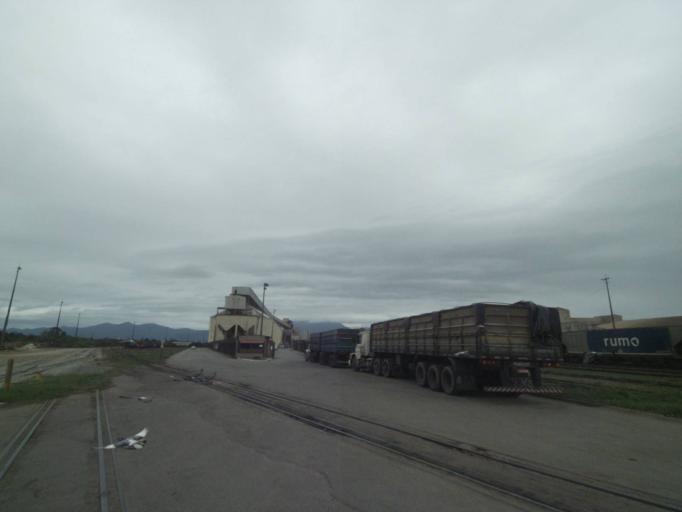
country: BR
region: Parana
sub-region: Paranagua
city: Paranagua
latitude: -25.5392
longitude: -48.5385
